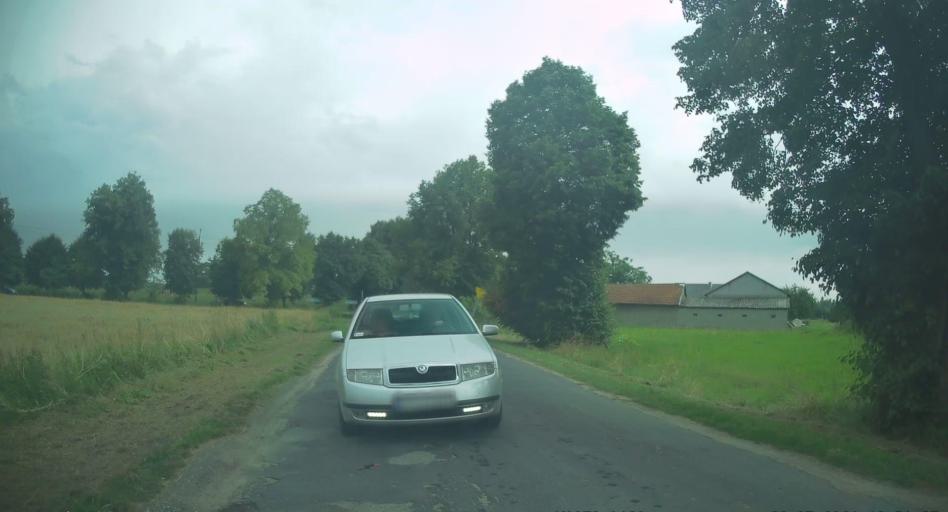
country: PL
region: Lodz Voivodeship
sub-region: Powiat rawski
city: Rawa Mazowiecka
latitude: 51.7502
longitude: 20.1880
